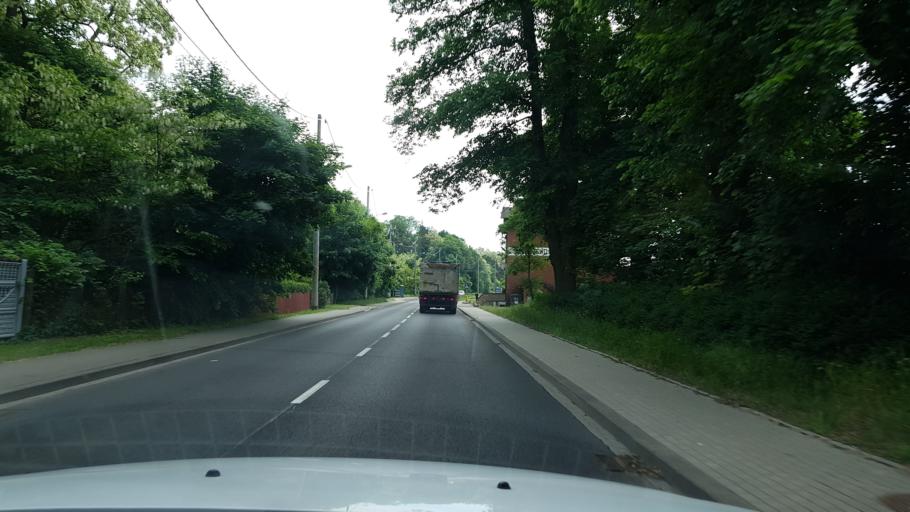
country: PL
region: West Pomeranian Voivodeship
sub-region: Powiat gryfinski
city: Gryfino
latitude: 53.3070
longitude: 14.5298
